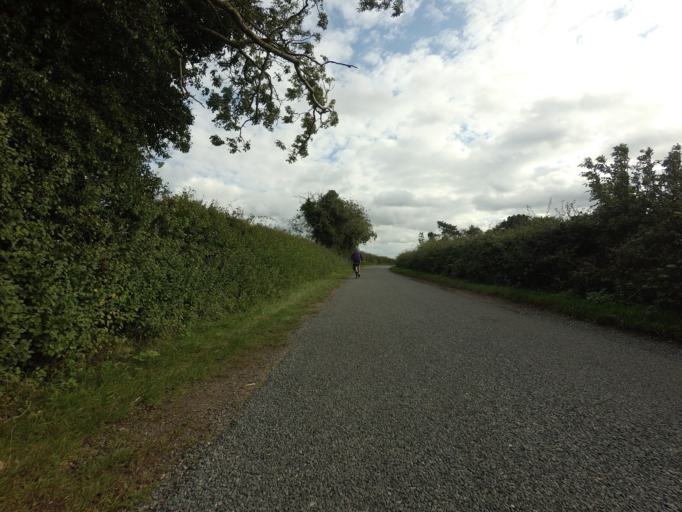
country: GB
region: England
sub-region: Norfolk
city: Dersingham
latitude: 52.8559
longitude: 0.5168
